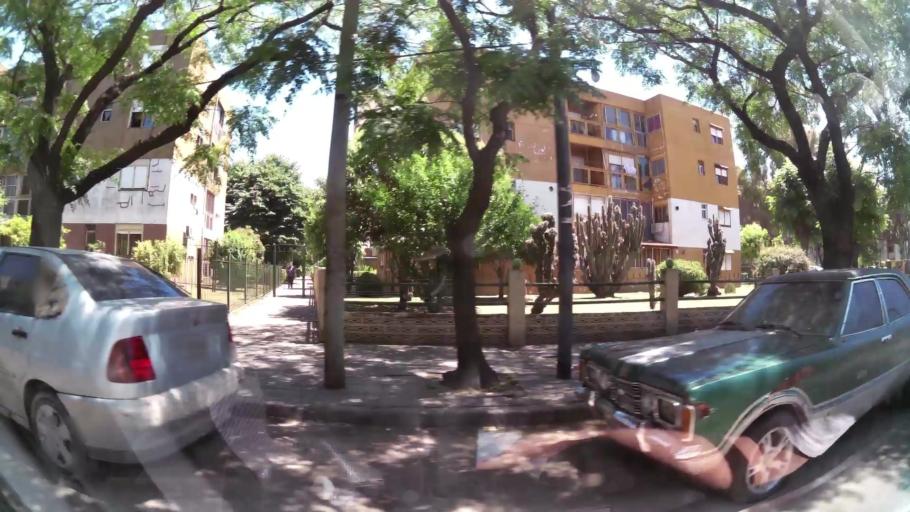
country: AR
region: Buenos Aires
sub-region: Partido de Avellaneda
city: Avellaneda
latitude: -34.6553
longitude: -58.4031
